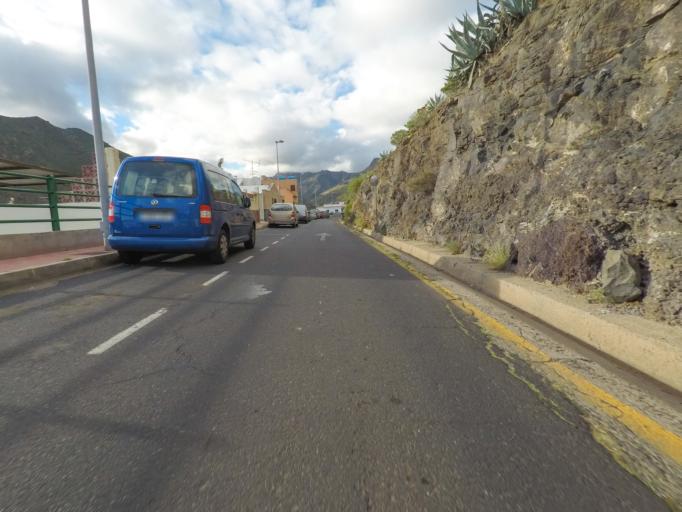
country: ES
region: Canary Islands
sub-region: Provincia de Santa Cruz de Tenerife
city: San Sebastian de la Gomera
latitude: 28.0952
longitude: -17.1126
